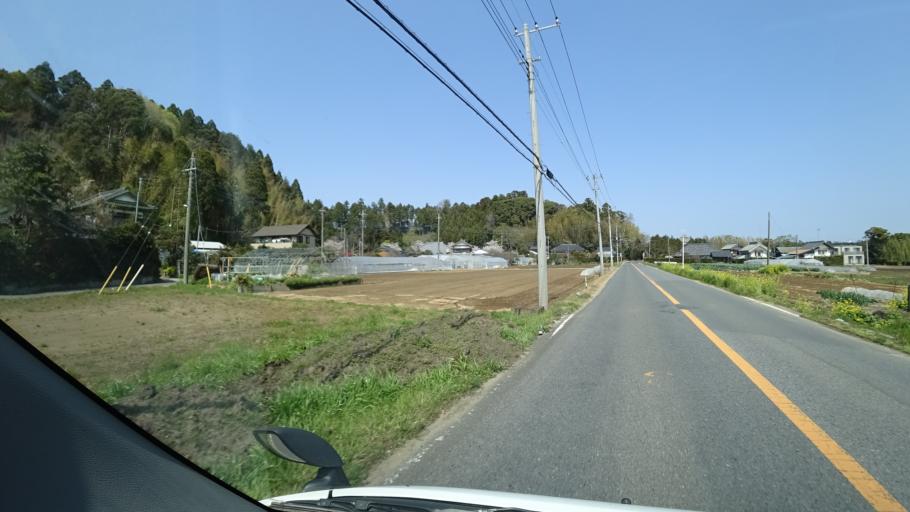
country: JP
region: Chiba
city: Yokaichiba
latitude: 35.6832
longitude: 140.4631
